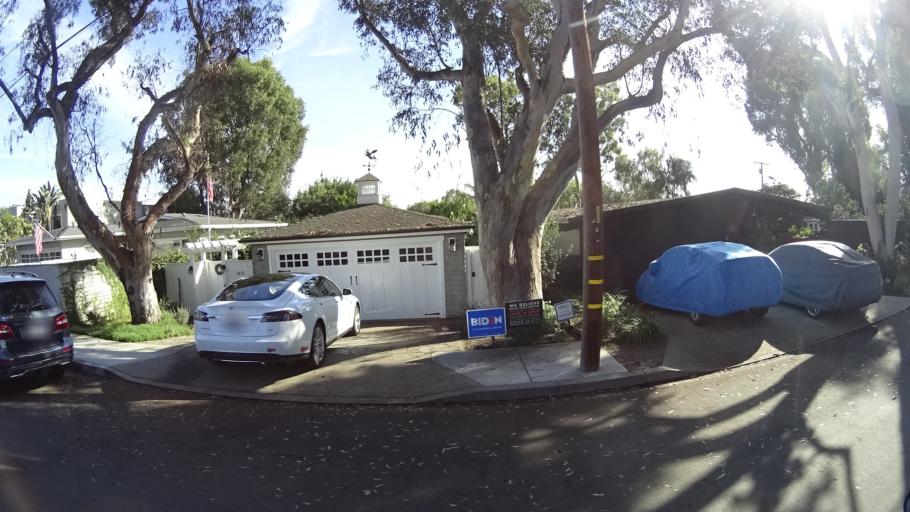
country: US
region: California
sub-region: Los Angeles County
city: Manhattan Beach
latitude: 33.8918
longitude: -118.4023
